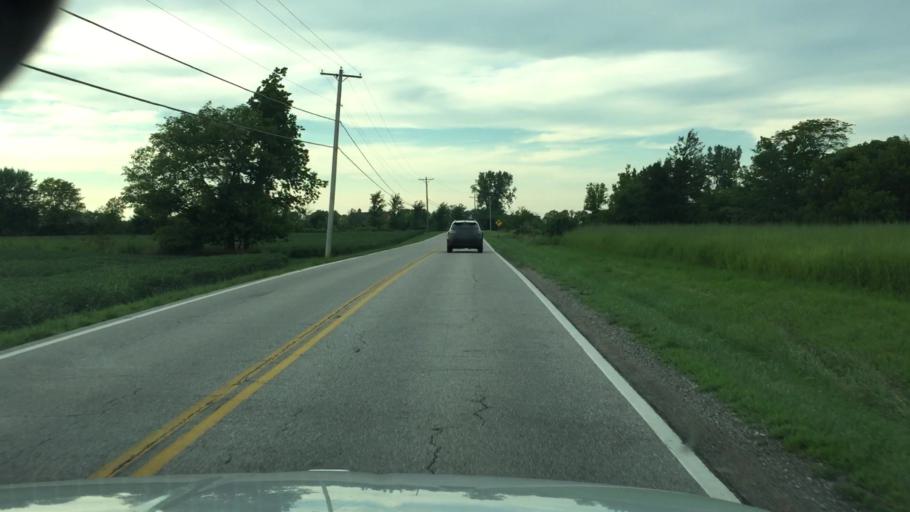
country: US
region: Ohio
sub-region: Madison County
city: West Jefferson
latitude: 39.9830
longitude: -83.2631
